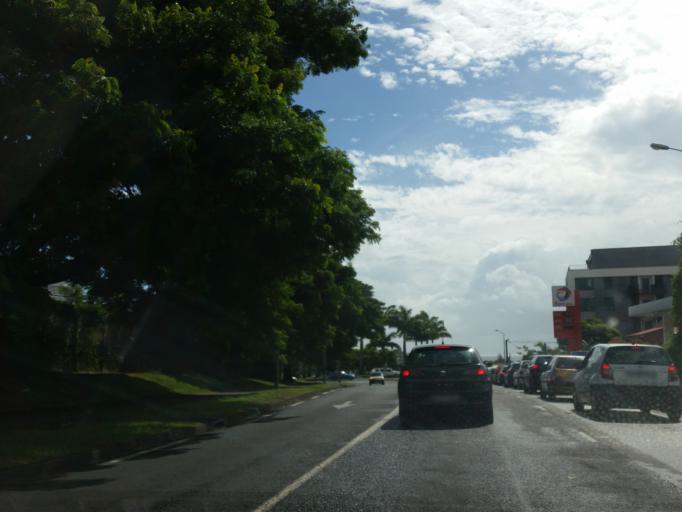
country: RE
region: Reunion
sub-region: Reunion
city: Sainte-Marie
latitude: -20.9035
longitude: 55.5034
